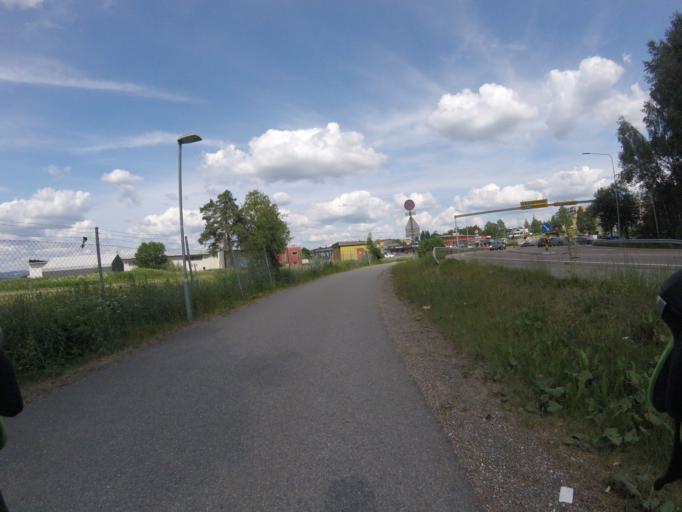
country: NO
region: Akershus
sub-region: Skedsmo
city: Lillestrom
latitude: 59.9670
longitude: 11.0517
